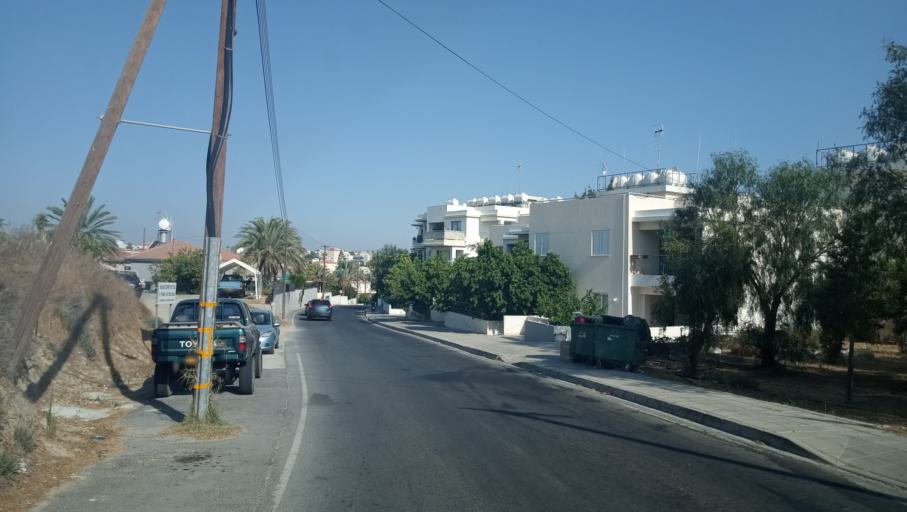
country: CY
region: Lefkosia
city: Geri
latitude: 35.1040
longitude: 33.4243
